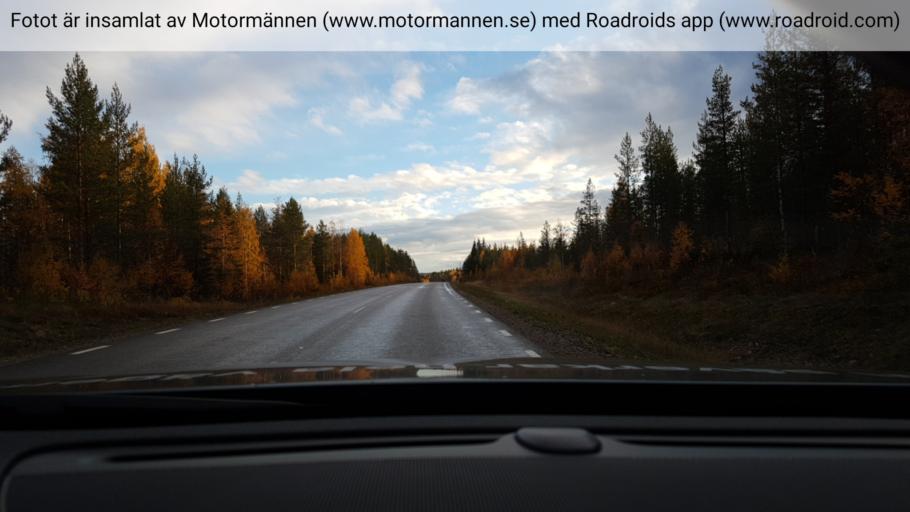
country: SE
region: Norrbotten
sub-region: Overkalix Kommun
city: OEverkalix
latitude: 66.7418
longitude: 22.6704
